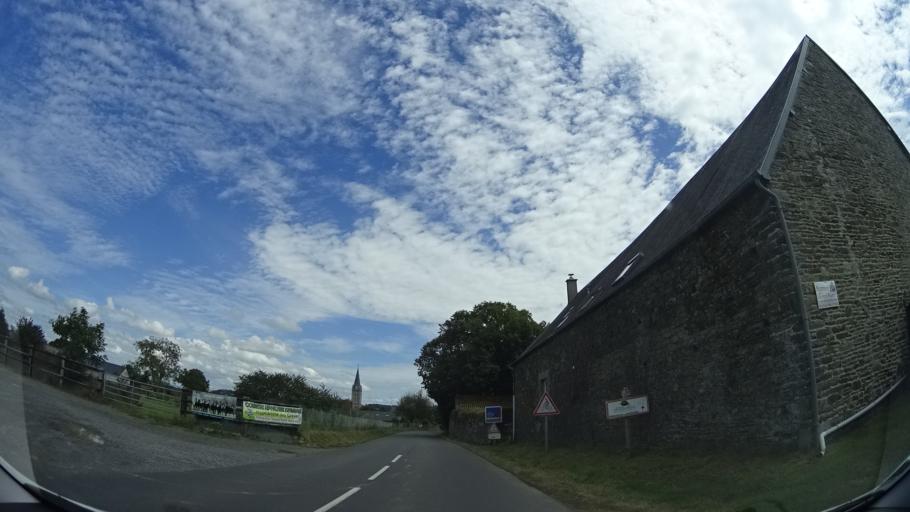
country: FR
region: Lower Normandy
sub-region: Departement de la Manche
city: Marcey-les-Greves
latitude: 48.6824
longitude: -1.4149
